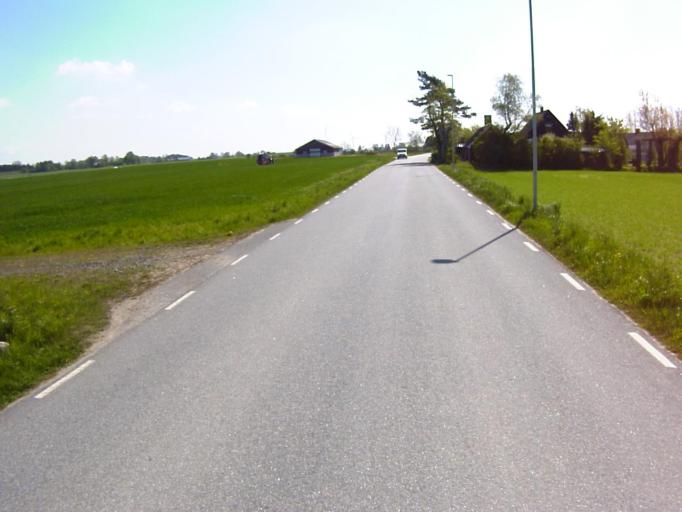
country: SE
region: Skane
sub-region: Kristianstads Kommun
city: Kristianstad
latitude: 56.0206
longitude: 14.2178
